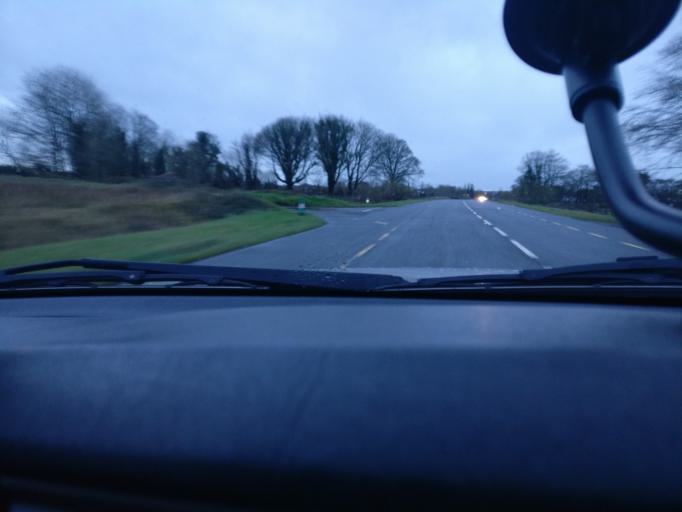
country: IE
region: Connaught
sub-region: County Galway
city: Ballinasloe
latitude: 53.2943
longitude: -8.3286
